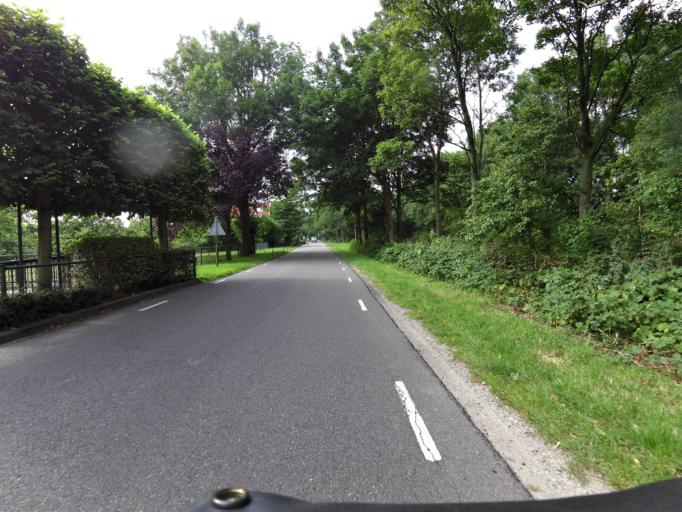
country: NL
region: South Holland
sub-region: Gemeente Maassluis
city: Maassluis
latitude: 51.8675
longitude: 4.2476
